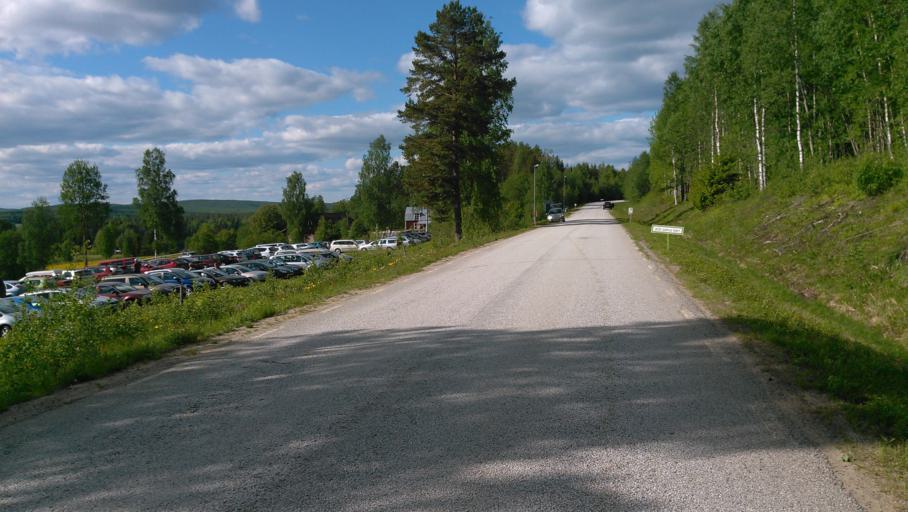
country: SE
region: Vaesterbotten
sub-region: Vannas Kommun
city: Vannasby
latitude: 64.0037
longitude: 19.9188
